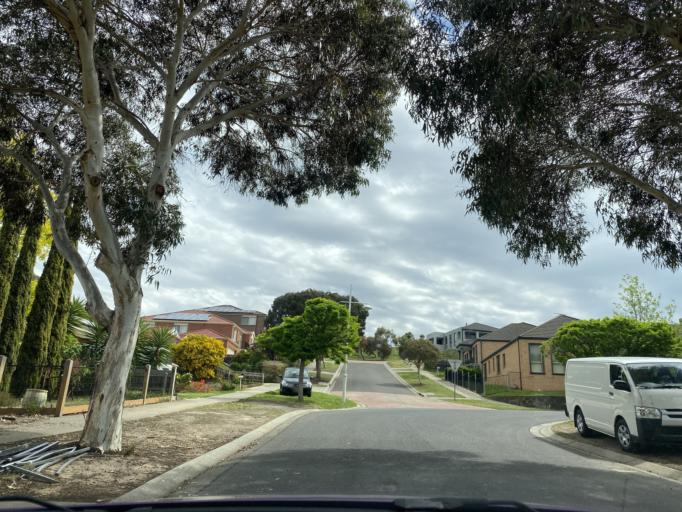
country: AU
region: Victoria
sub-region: Whittlesea
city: Mill Park
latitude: -37.6357
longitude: 145.0642
